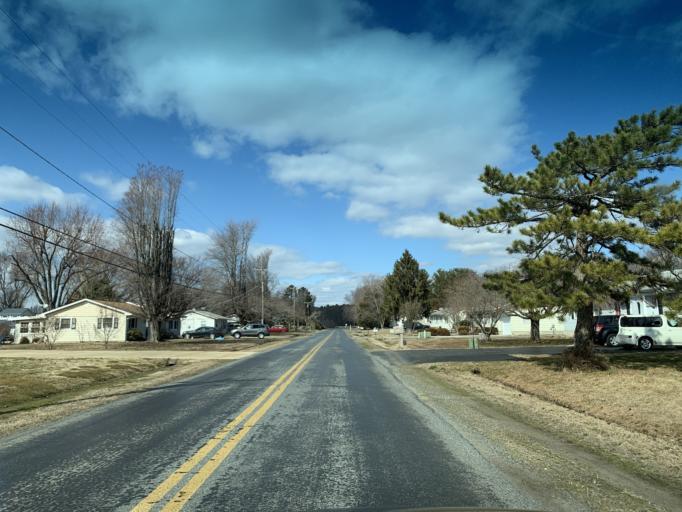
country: US
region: Maryland
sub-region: Queen Anne's County
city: Chester
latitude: 38.9378
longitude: -76.2660
